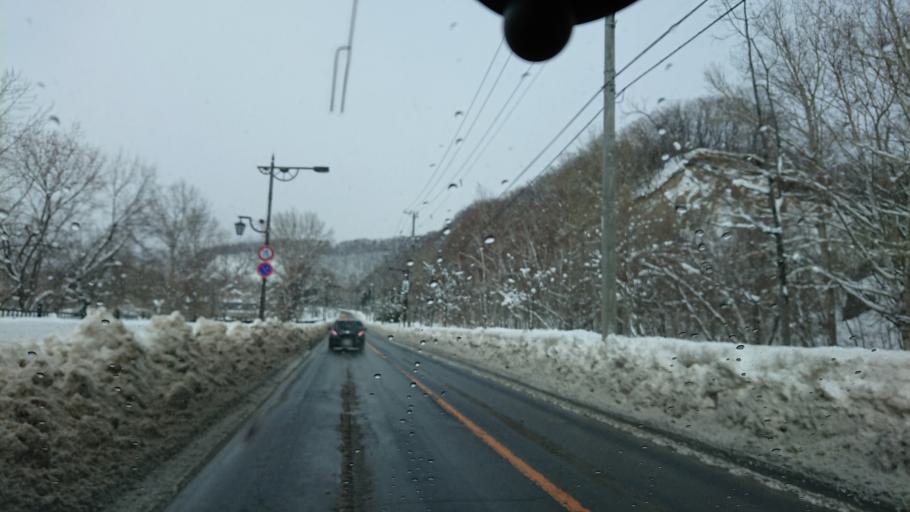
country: JP
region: Hokkaido
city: Sapporo
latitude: 42.9780
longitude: 141.3441
